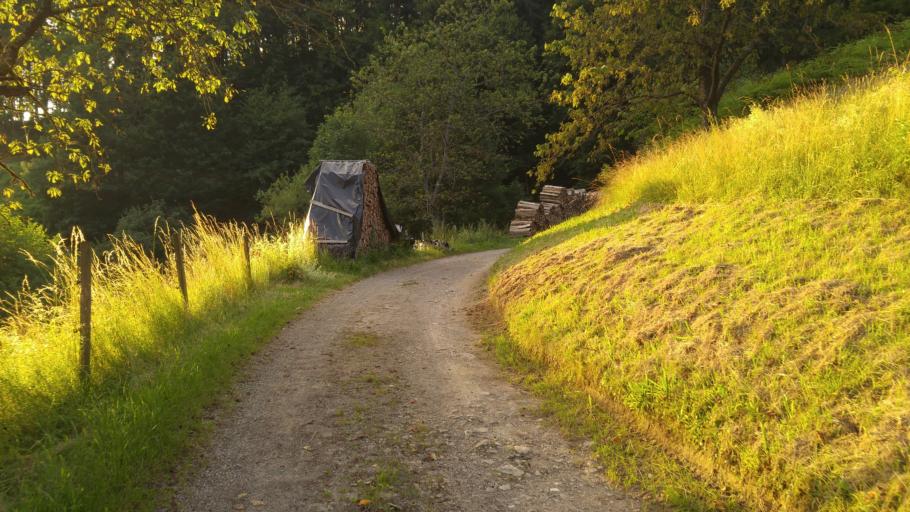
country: DE
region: Baden-Wuerttemberg
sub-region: Freiburg Region
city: Muenstertal/Schwarzwald
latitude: 47.8483
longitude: 7.7963
